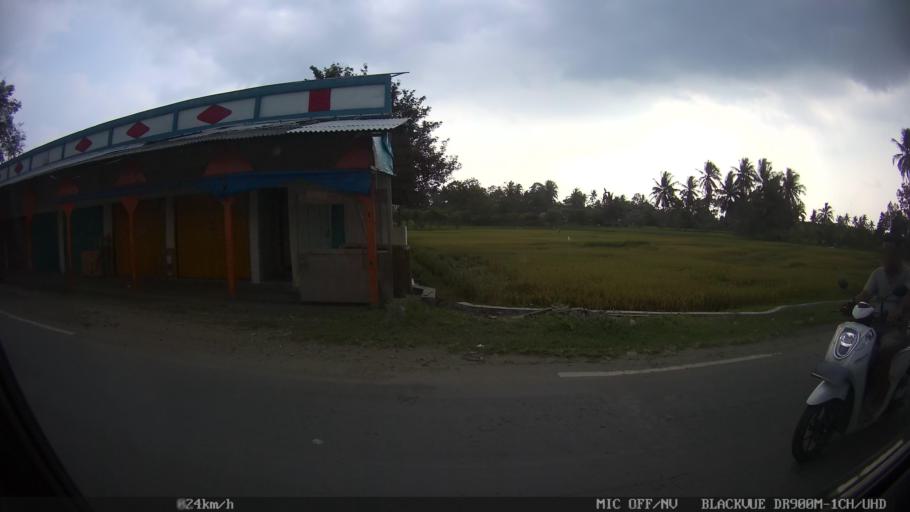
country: ID
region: Lampung
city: Gedongtataan
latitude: -5.3785
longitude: 105.0935
